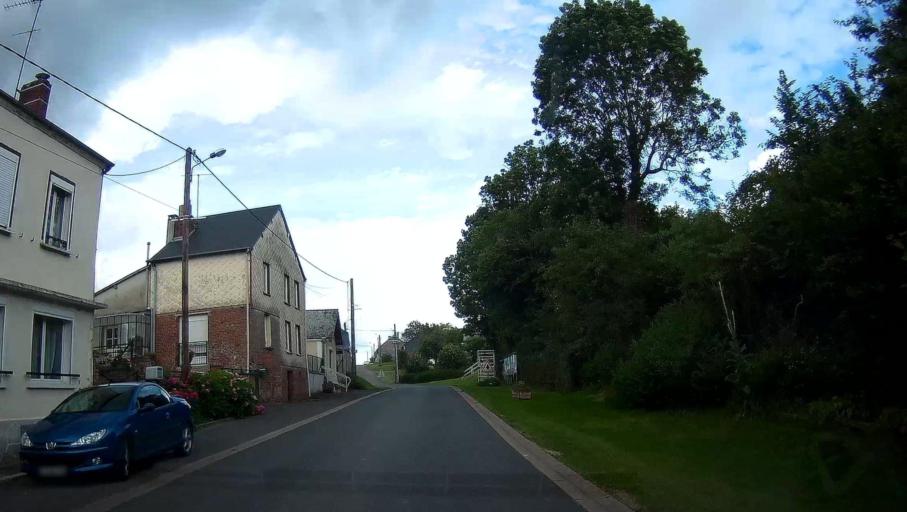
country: FR
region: Picardie
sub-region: Departement de l'Aisne
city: Rozoy-sur-Serre
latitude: 49.7250
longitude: 4.3075
